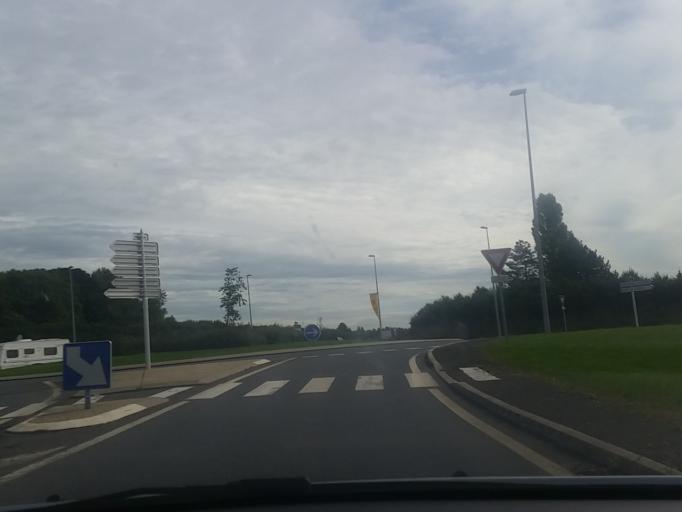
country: FR
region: Pays de la Loire
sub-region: Departement de la Loire-Atlantique
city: Chateaubriant
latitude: 47.7002
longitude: -1.3823
